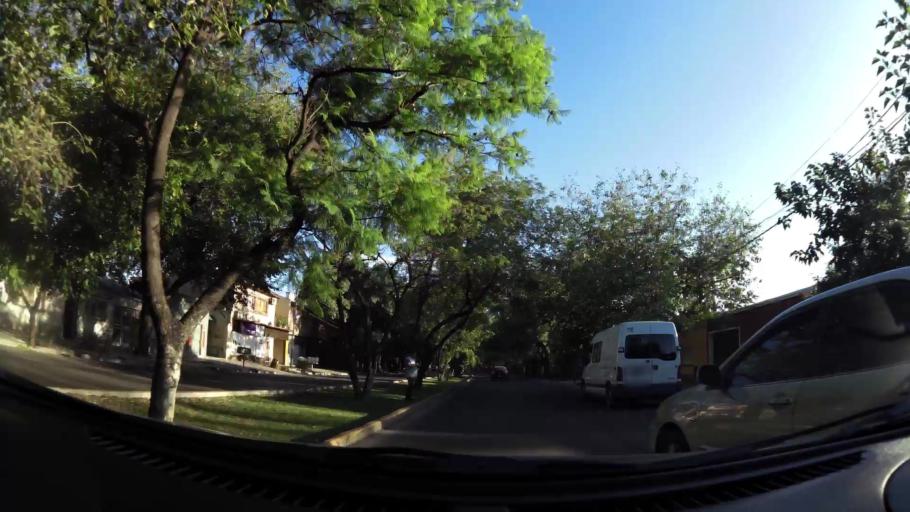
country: AR
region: Mendoza
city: Las Heras
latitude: -32.8651
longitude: -68.8383
